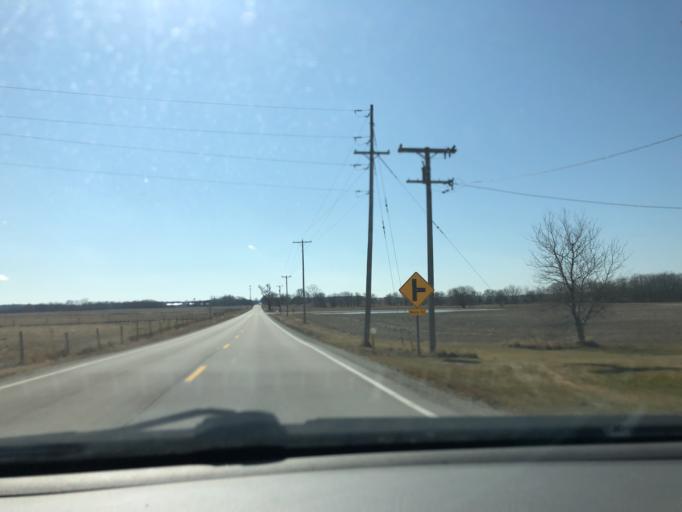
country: US
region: Illinois
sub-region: Kane County
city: Hampshire
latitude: 42.1348
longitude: -88.5351
